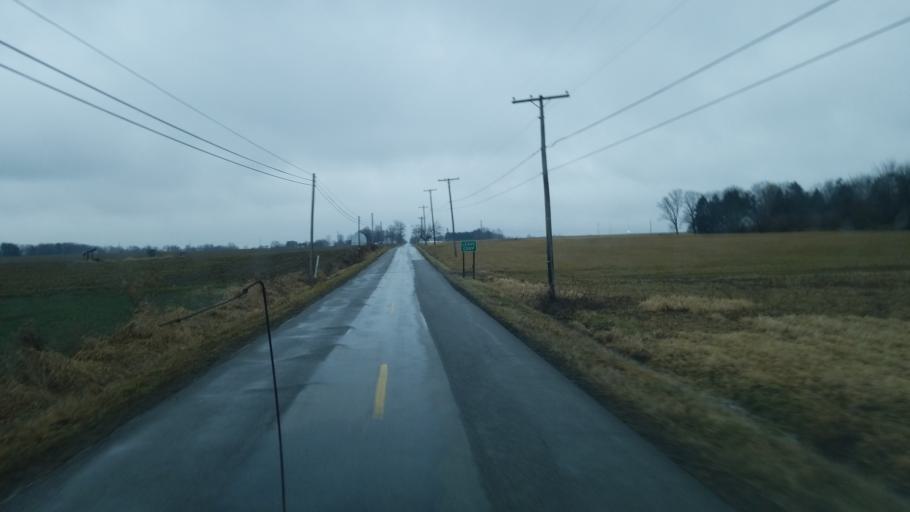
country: US
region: Ohio
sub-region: Wayne County
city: Smithville
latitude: 40.8516
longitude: -81.8616
